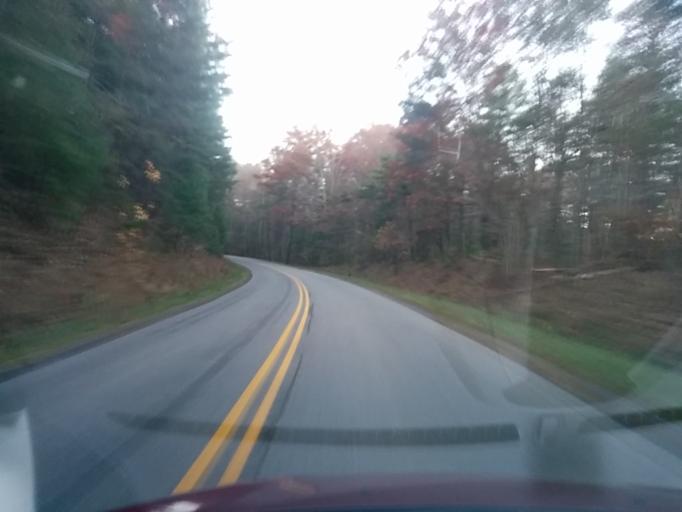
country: US
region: Virginia
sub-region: City of Lexington
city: Lexington
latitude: 37.9387
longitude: -79.5715
